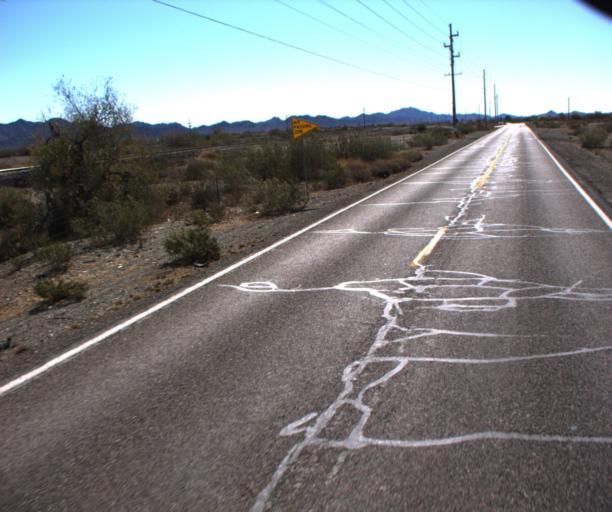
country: US
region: Arizona
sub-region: La Paz County
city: Salome
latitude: 33.7493
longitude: -113.7662
